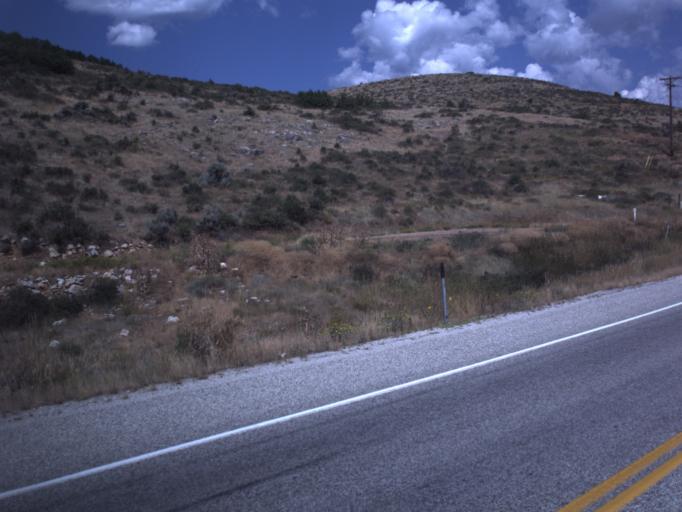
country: US
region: Idaho
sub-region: Bear Lake County
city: Paris
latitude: 41.9406
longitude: -111.4102
